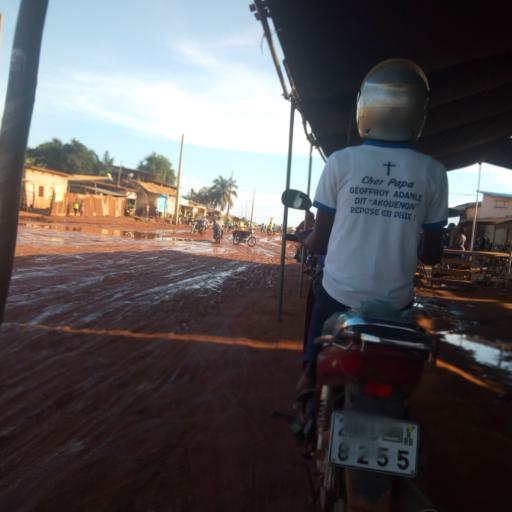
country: BJ
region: Atlantique
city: Hevie
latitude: 6.4003
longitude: 2.2691
